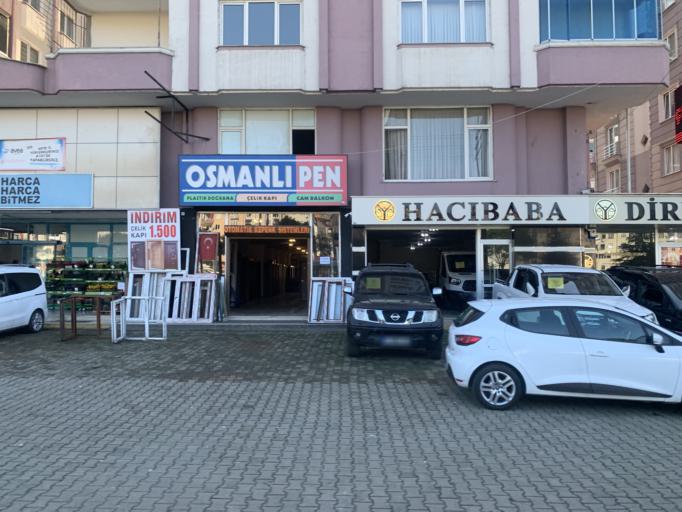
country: TR
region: Trabzon
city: Of
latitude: 40.9423
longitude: 40.2673
